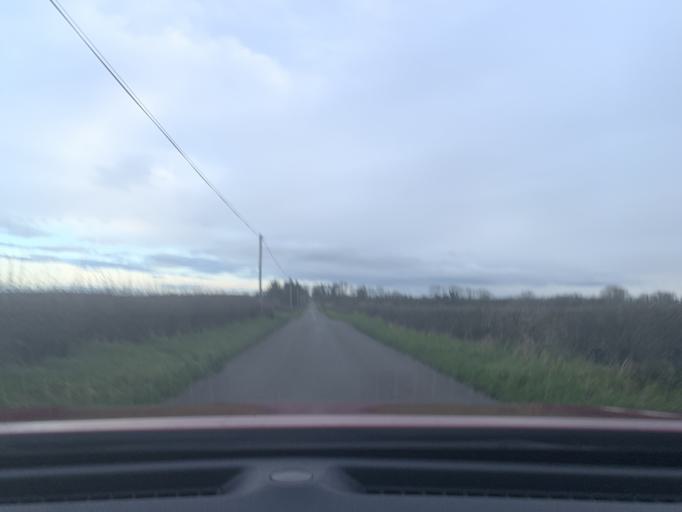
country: IE
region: Connaught
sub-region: Roscommon
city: Ballaghaderreen
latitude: 53.8796
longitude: -8.5633
